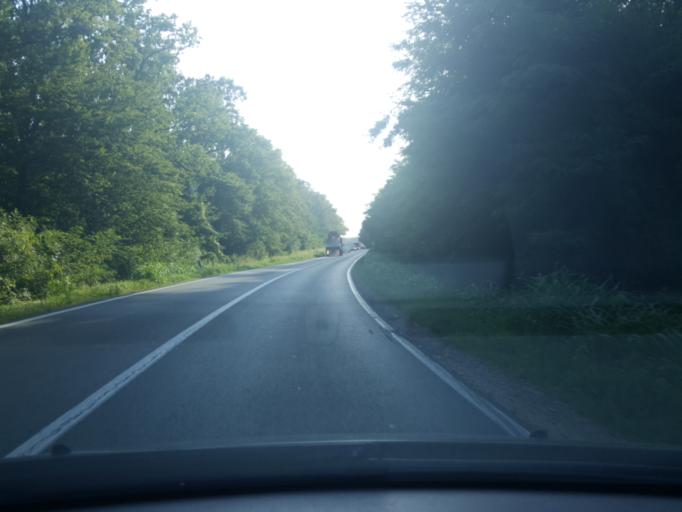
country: RS
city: Klenak
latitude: 44.8077
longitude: 19.7496
